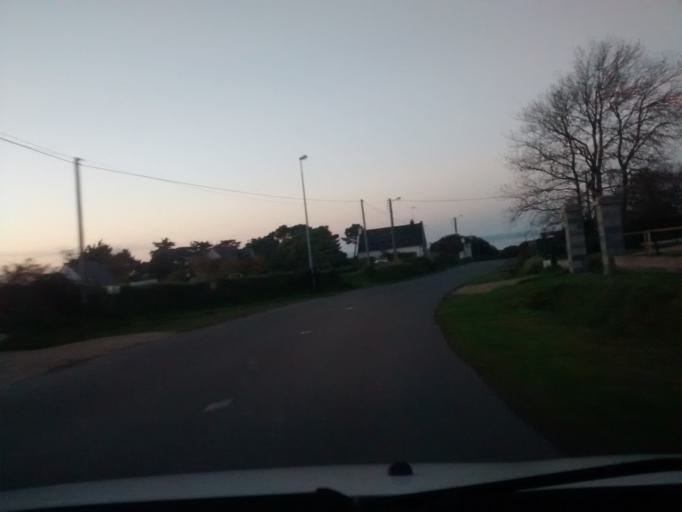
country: FR
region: Brittany
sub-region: Departement des Cotes-d'Armor
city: Trevou-Treguignec
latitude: 48.8168
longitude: -3.3379
